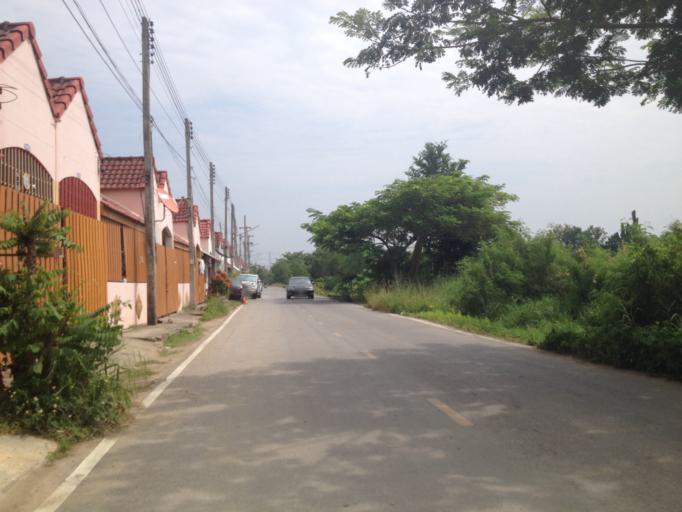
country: TH
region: Chiang Mai
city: San Pa Tong
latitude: 18.6549
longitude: 98.9020
